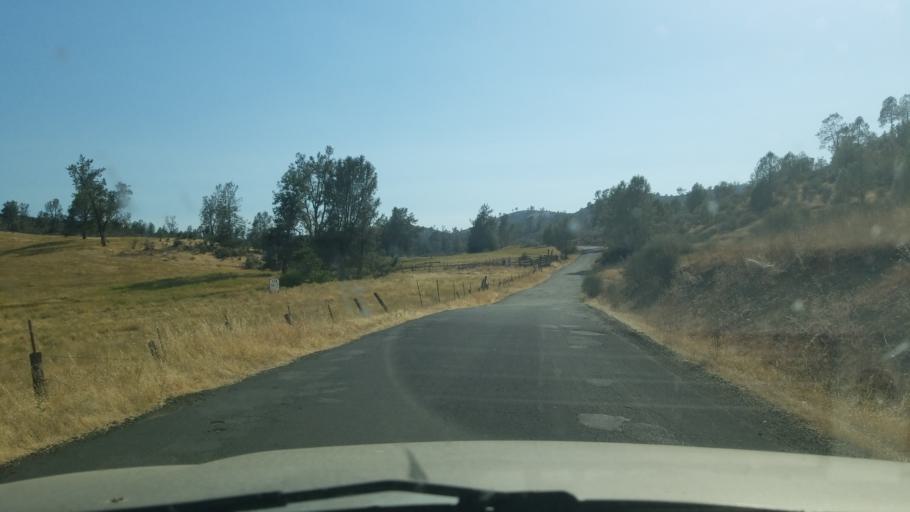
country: US
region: California
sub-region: Tuolumne County
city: Jamestown
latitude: 37.8508
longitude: -120.4541
